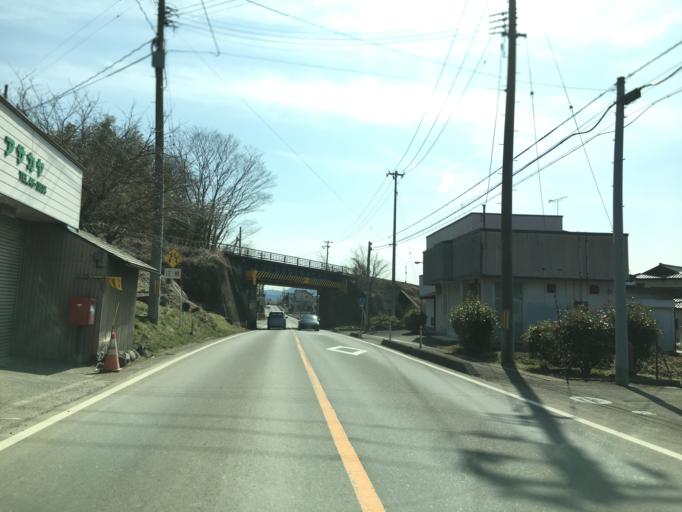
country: JP
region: Ibaraki
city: Daigo
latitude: 36.9161
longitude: 140.4168
